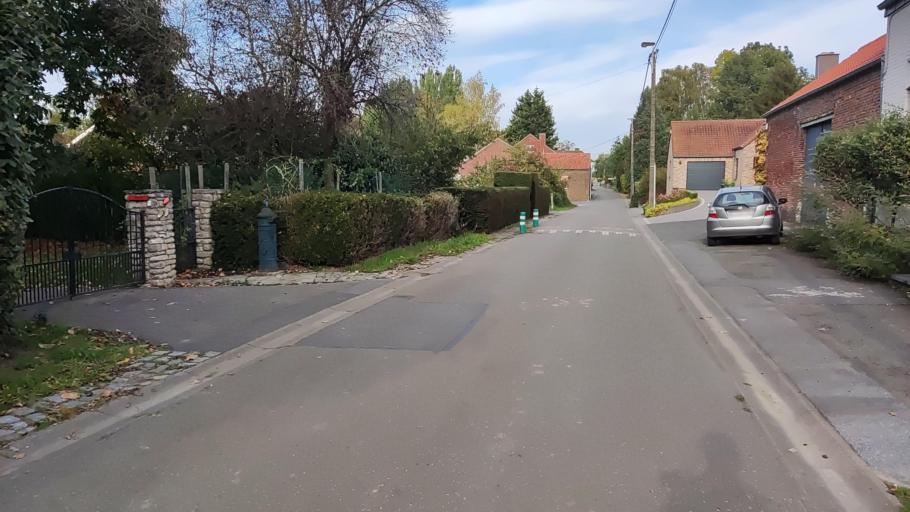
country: BE
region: Wallonia
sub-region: Province du Brabant Wallon
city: Jodoigne
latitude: 50.7455
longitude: 4.8758
